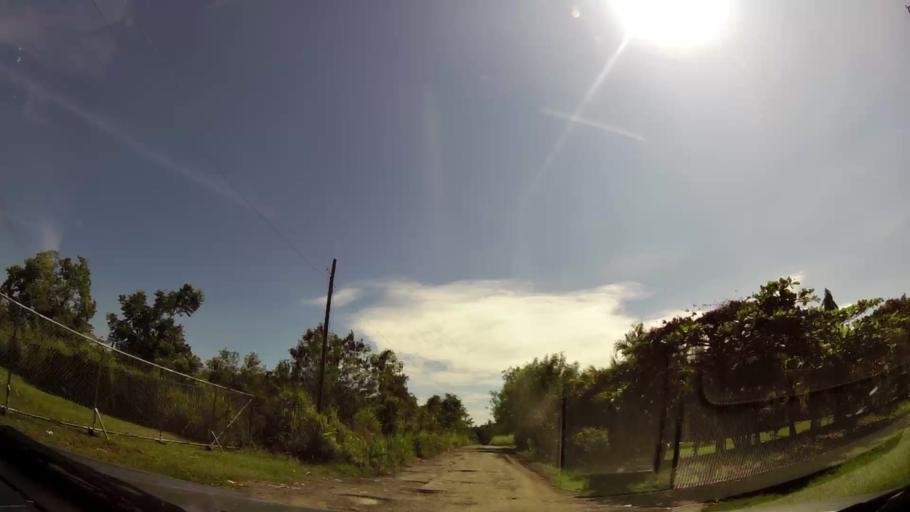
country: PA
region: Panama
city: Nueva Gorgona
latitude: 8.5570
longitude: -79.8699
